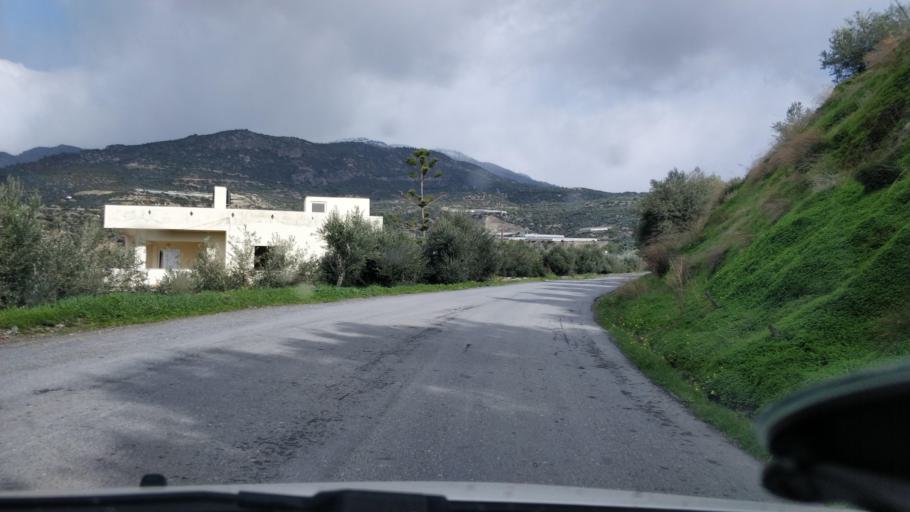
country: GR
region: Crete
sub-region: Nomos Lasithiou
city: Gra Liyia
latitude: 34.9885
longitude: 25.5003
